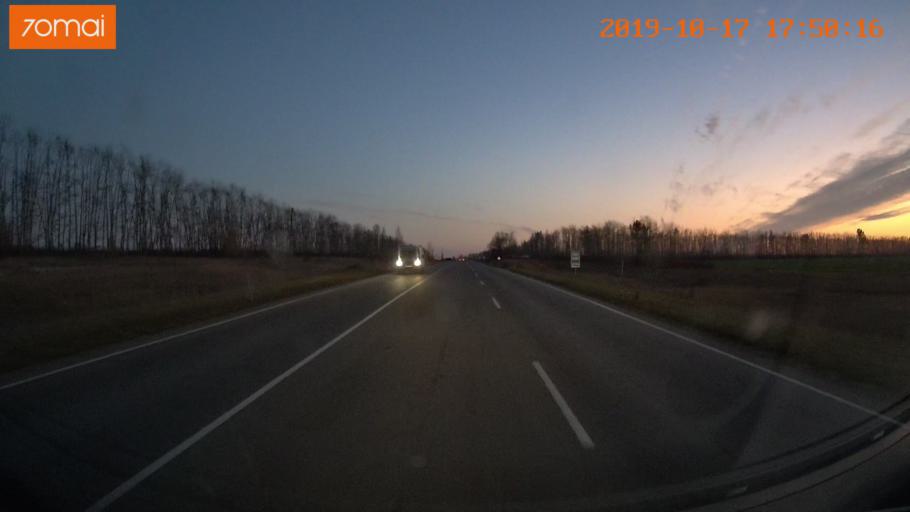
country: RU
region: Tula
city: Yepifan'
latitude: 53.6662
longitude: 38.6869
